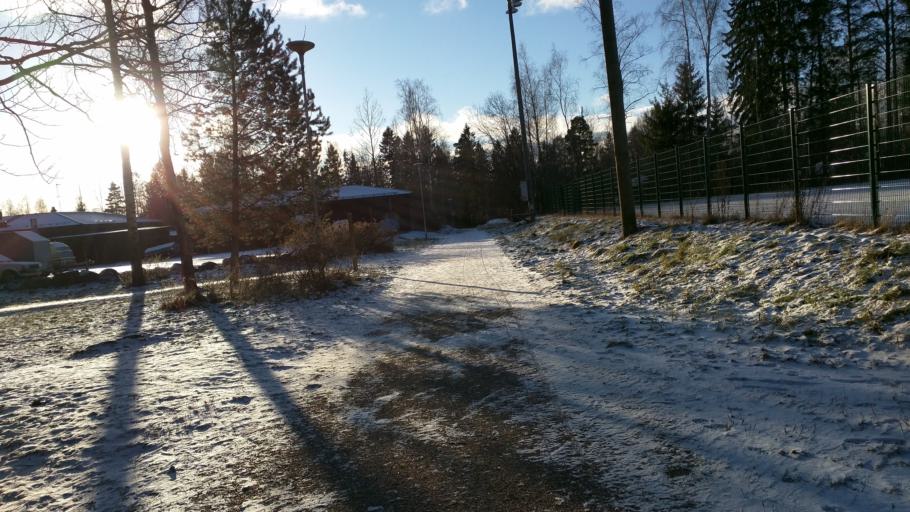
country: FI
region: Uusimaa
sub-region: Helsinki
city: Kilo
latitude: 60.2437
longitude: 24.7652
